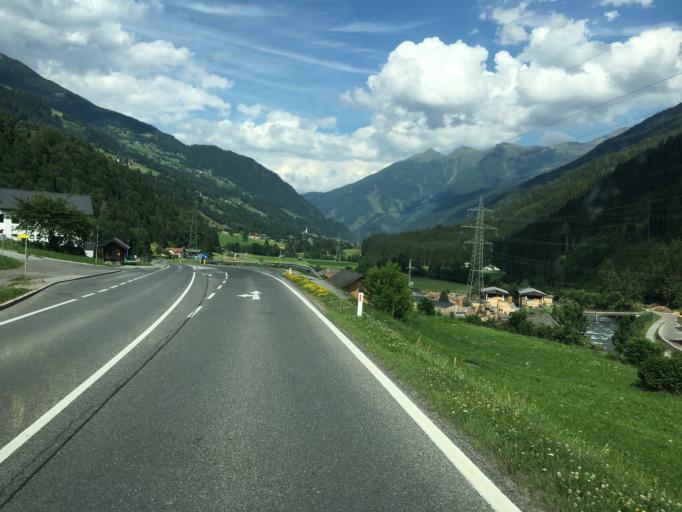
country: AT
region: Carinthia
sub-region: Politischer Bezirk Spittal an der Drau
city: Rangersdorf
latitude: 46.8727
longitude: 12.9942
